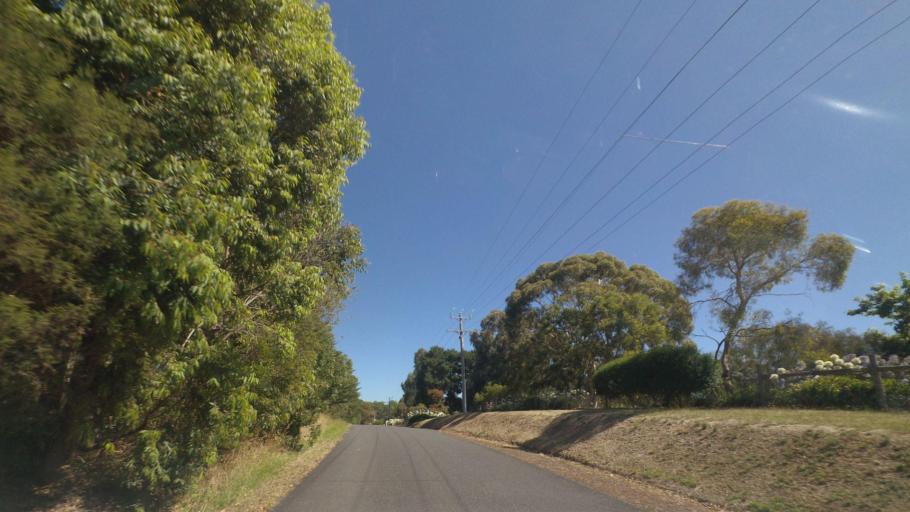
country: AU
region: Victoria
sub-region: Yarra Ranges
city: Chirnside Park
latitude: -37.7399
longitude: 145.3244
